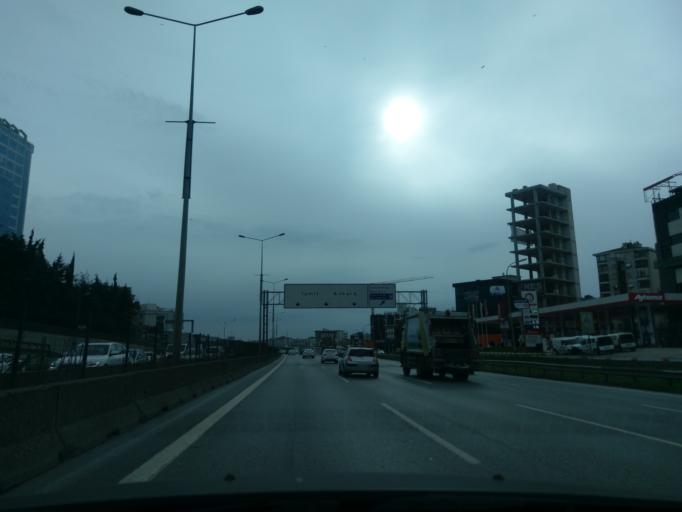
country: TR
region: Istanbul
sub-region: Atasehir
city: Atasehir
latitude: 40.9684
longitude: 29.1027
